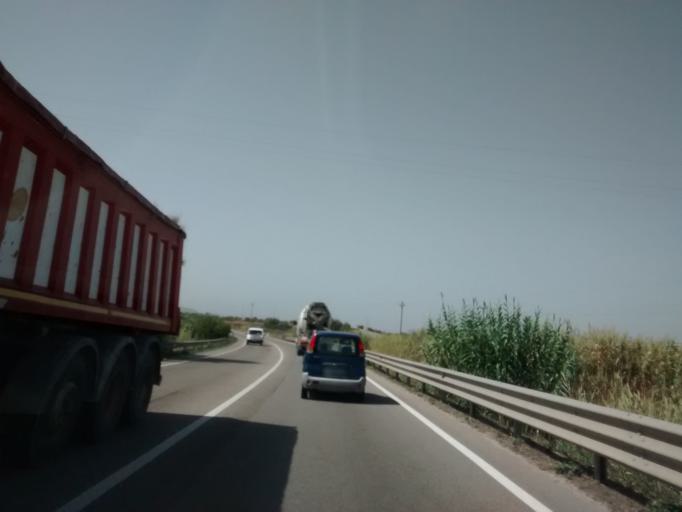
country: IT
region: Sardinia
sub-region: Provincia di Cagliari
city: Settimo San Pietro
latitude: 39.2693
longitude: 9.2039
